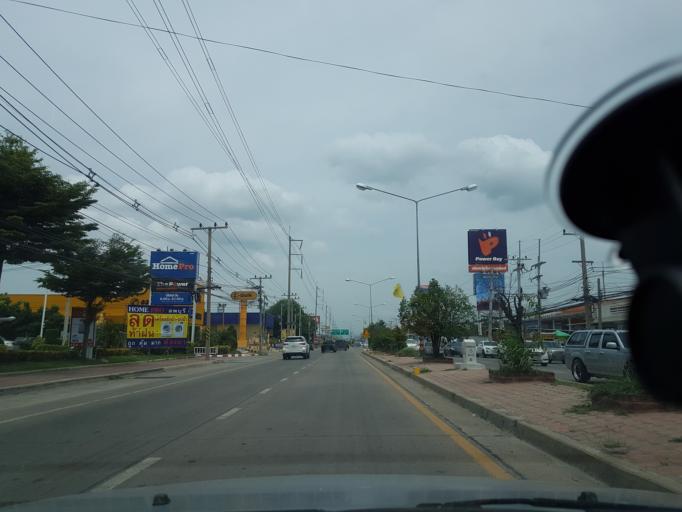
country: TH
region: Lop Buri
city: Lop Buri
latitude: 14.7838
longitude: 100.6835
